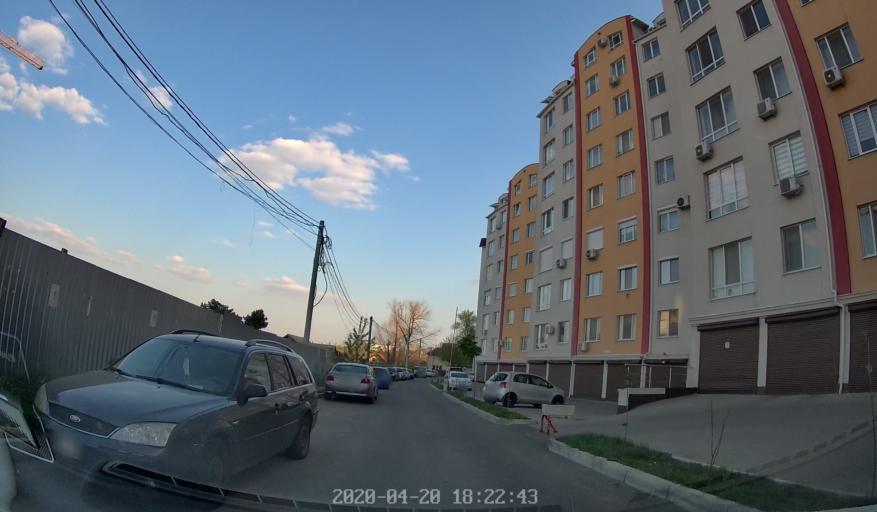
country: MD
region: Chisinau
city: Chisinau
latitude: 46.9971
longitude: 28.8367
